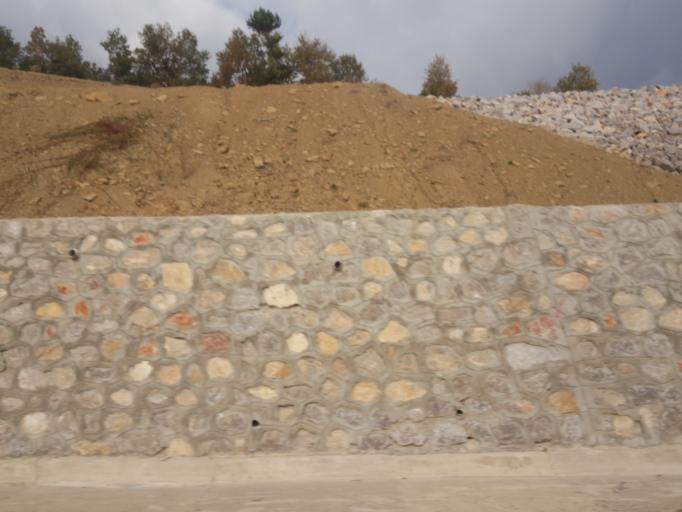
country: TR
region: Sinop
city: Duragan
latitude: 41.4889
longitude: 35.0384
